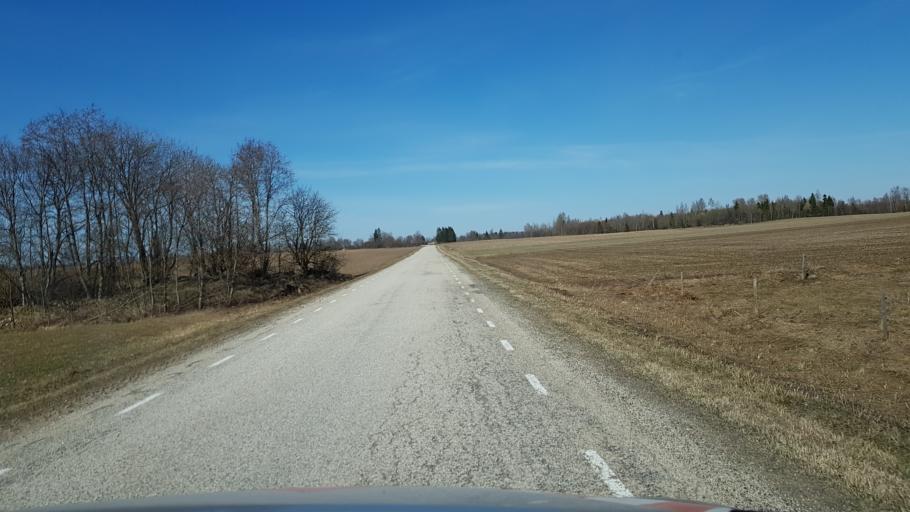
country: EE
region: Laeaene-Virumaa
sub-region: Vinni vald
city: Vinni
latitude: 59.0796
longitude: 26.5482
